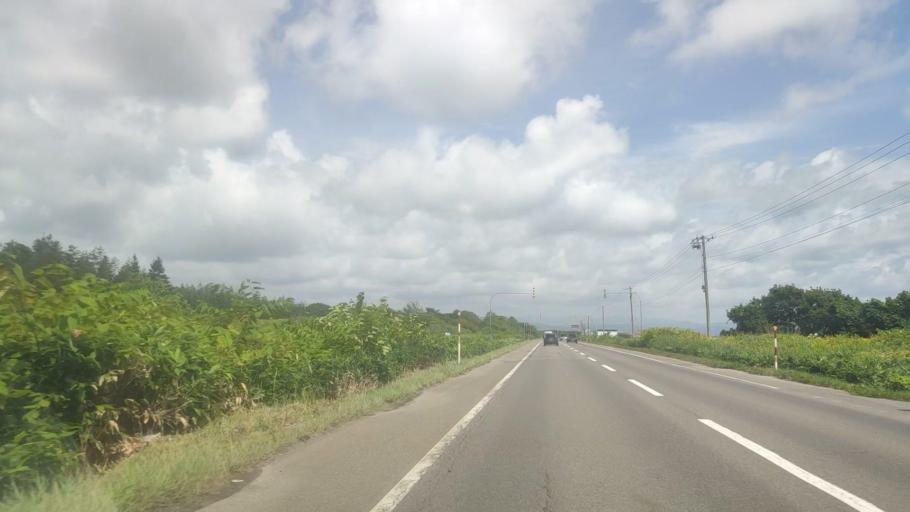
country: JP
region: Hokkaido
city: Niseko Town
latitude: 42.4816
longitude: 140.3509
